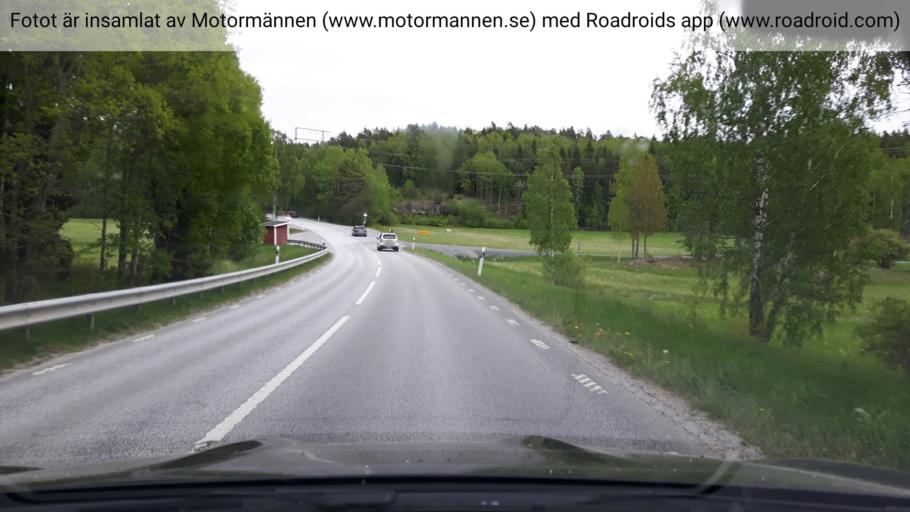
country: SE
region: Stockholm
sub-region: Osterakers Kommun
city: Akersberga
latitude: 59.5047
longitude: 18.3615
